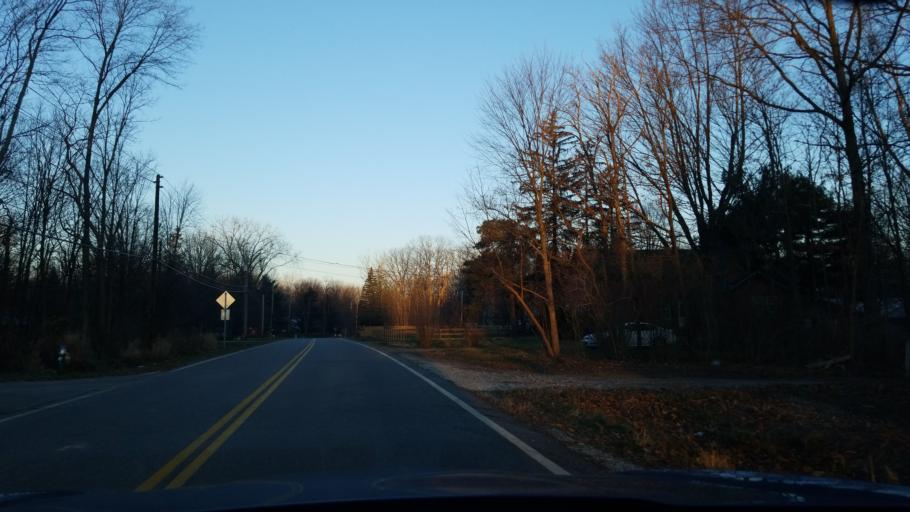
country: US
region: Ohio
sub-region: Cuyahoga County
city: Olmsted Falls
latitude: 41.3893
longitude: -81.8795
